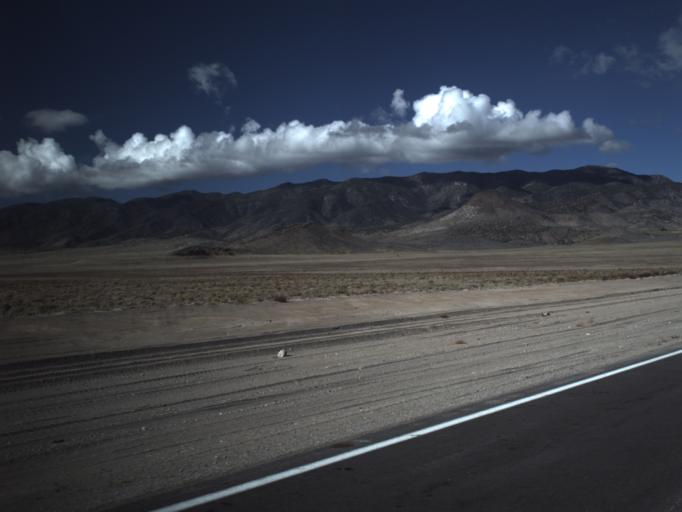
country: US
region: Utah
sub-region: Beaver County
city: Milford
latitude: 38.4783
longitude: -113.4310
